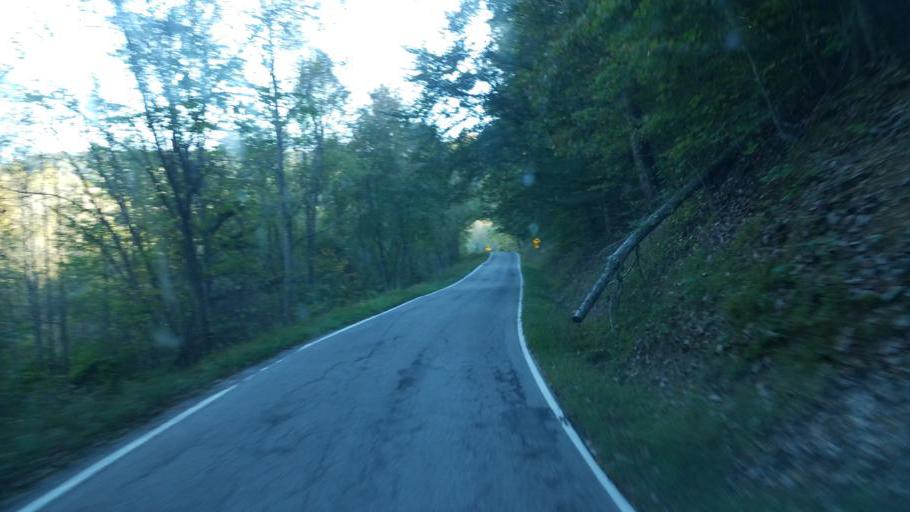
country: US
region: Ohio
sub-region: Adams County
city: Manchester
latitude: 38.5140
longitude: -83.5073
